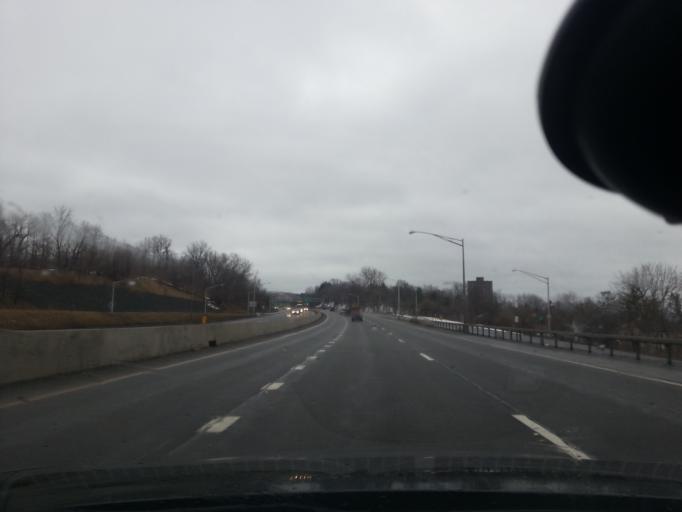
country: US
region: New York
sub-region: Onondaga County
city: Syracuse
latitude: 43.0159
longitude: -76.1398
